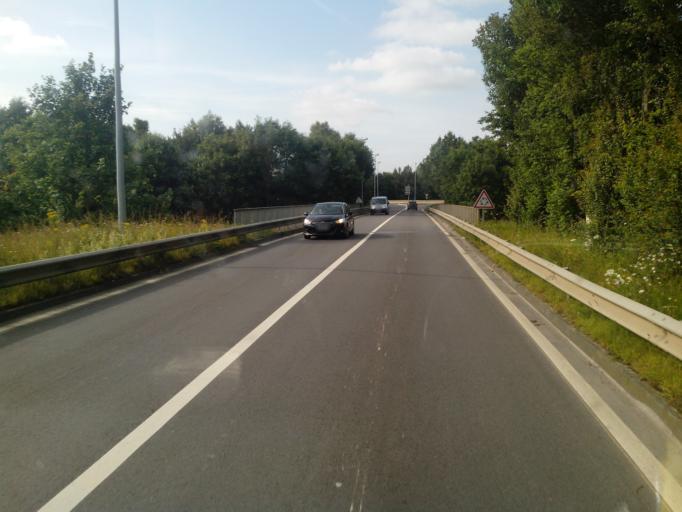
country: FR
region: Brittany
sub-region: Departement d'Ille-et-Vilaine
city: Le Rheu
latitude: 48.0786
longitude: -1.7937
